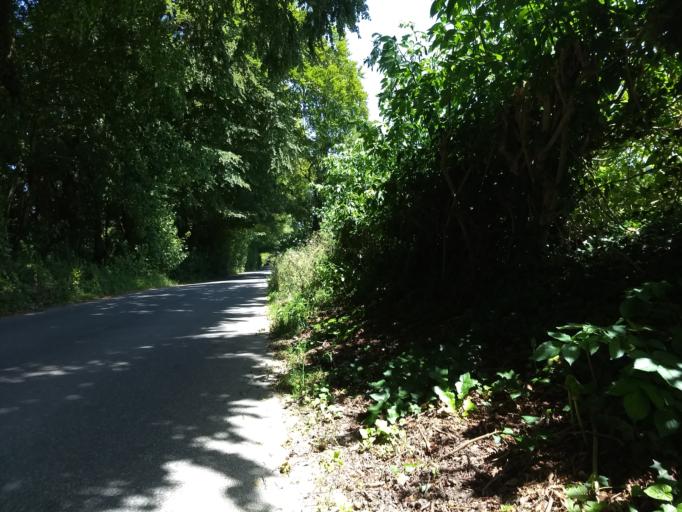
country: GB
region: England
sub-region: Isle of Wight
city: Shalfleet
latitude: 50.6712
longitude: -1.4016
